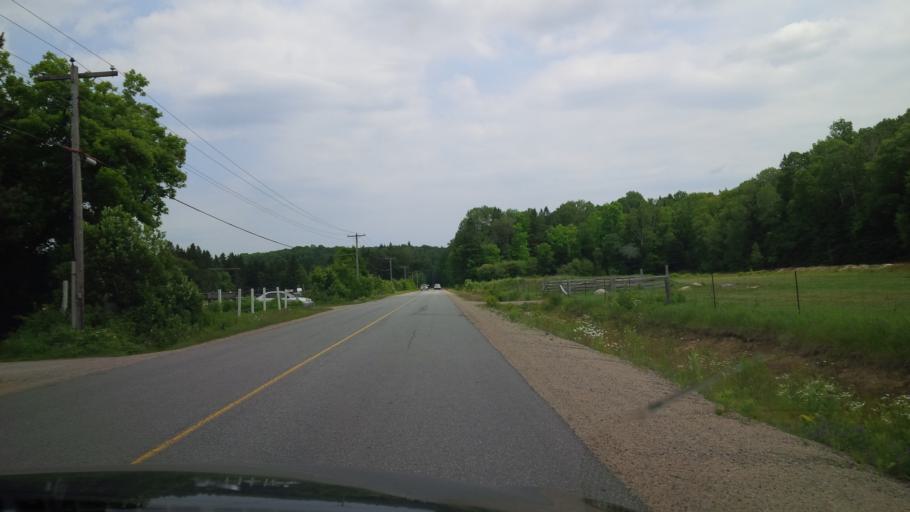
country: CA
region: Ontario
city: Huntsville
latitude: 45.6000
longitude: -79.1866
